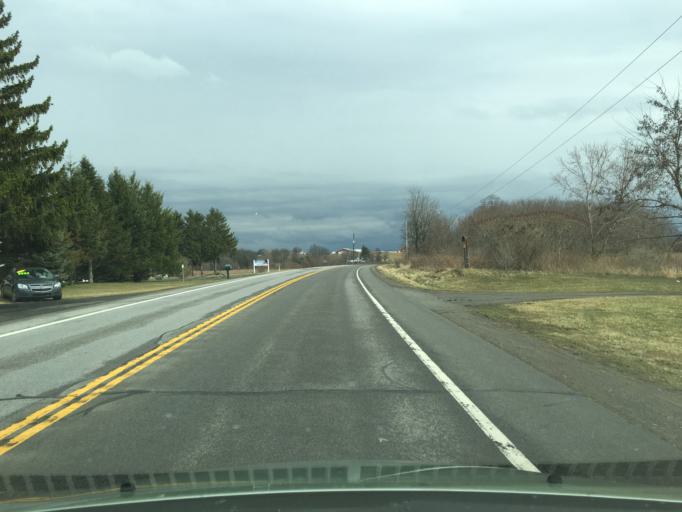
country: US
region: New York
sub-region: Wyoming County
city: Perry
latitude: 42.7317
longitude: -77.9800
